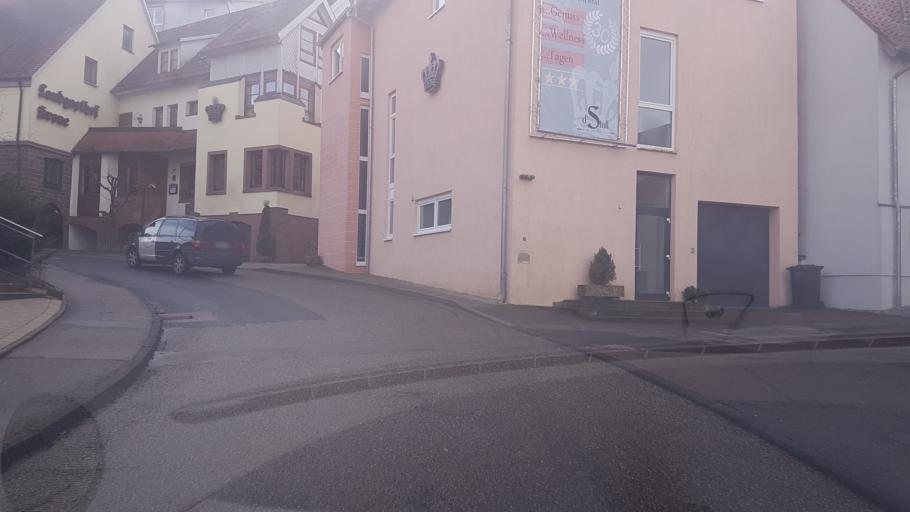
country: DE
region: Baden-Wuerttemberg
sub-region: Regierungsbezirk Stuttgart
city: Braunsbach
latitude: 49.2032
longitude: 9.7414
